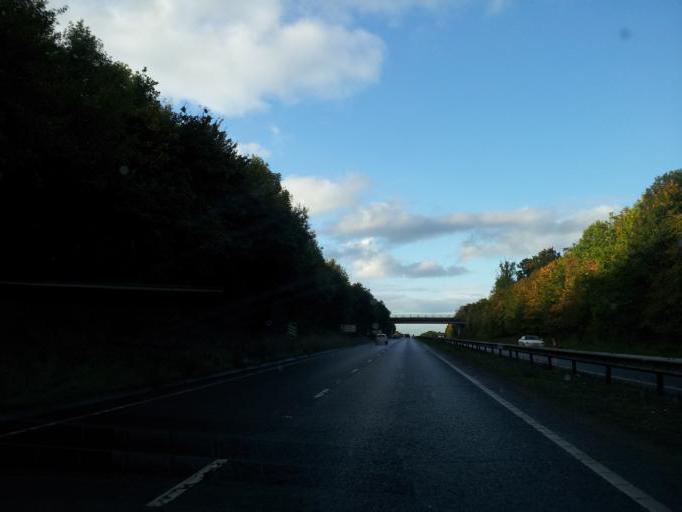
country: GB
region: England
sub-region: Norfolk
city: Thorpe Hamlet
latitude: 52.6124
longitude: 1.3321
